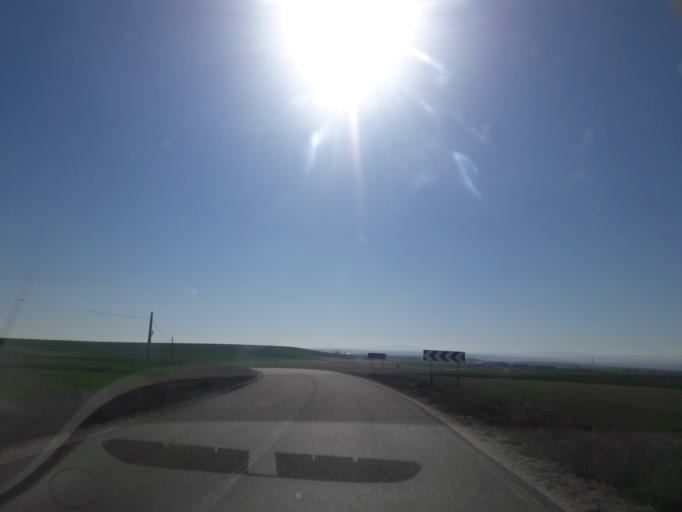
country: ES
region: Castille and Leon
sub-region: Provincia de Salamanca
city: Macotera
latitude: 40.8463
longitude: -5.3144
